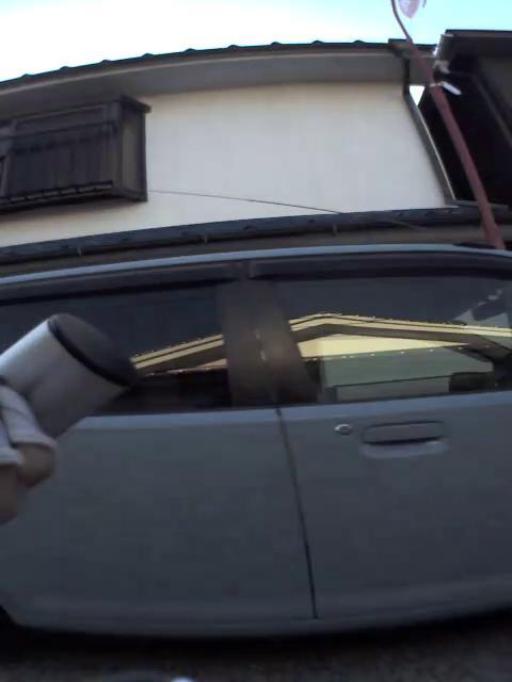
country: JP
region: Yamaguchi
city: Nagato
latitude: 34.3949
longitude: 131.1984
